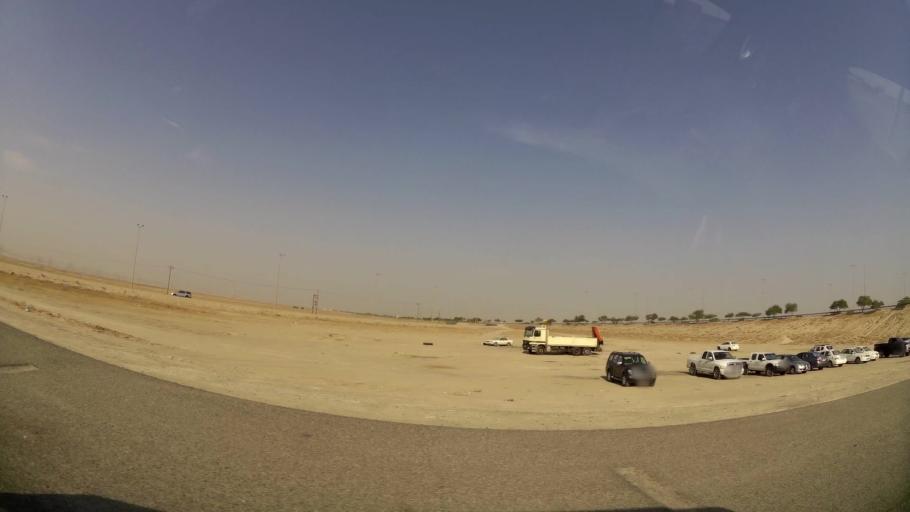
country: KW
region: Al Farwaniyah
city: Janub as Surrah
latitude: 29.1781
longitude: 47.9903
